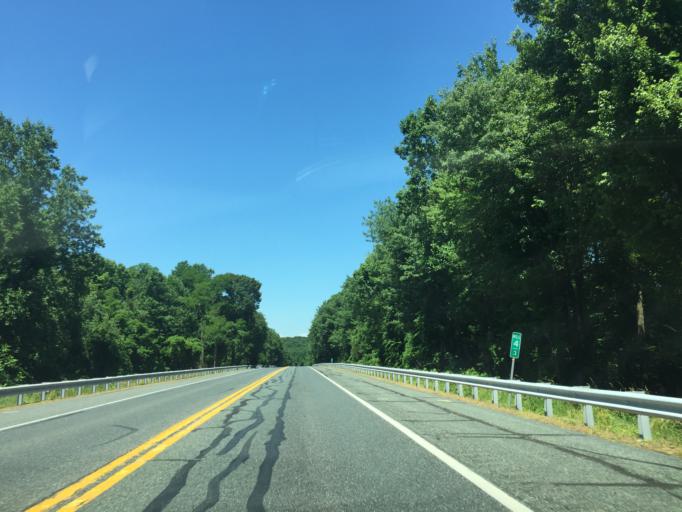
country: US
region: Maryland
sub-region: Harford County
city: Jarrettsville
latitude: 39.5752
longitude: -76.4292
